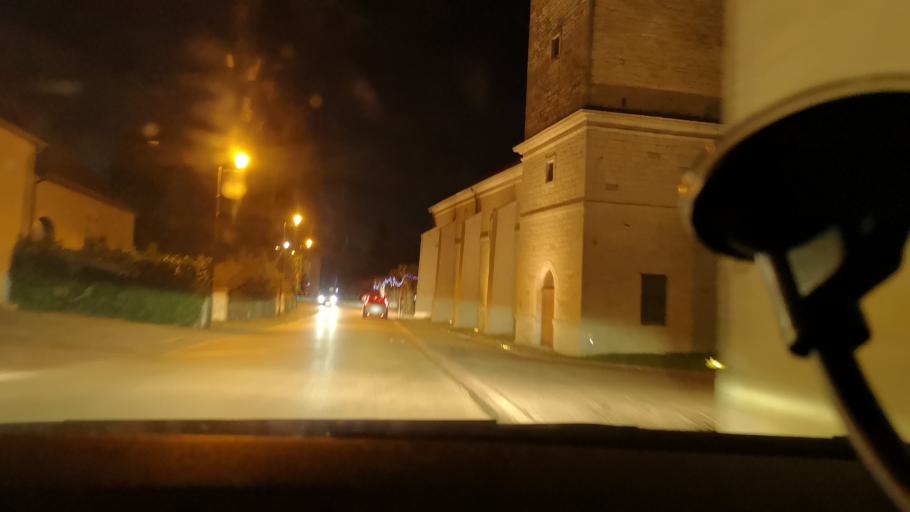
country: FR
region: Franche-Comte
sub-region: Departement du Jura
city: Bletterans
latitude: 46.7603
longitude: 5.5309
